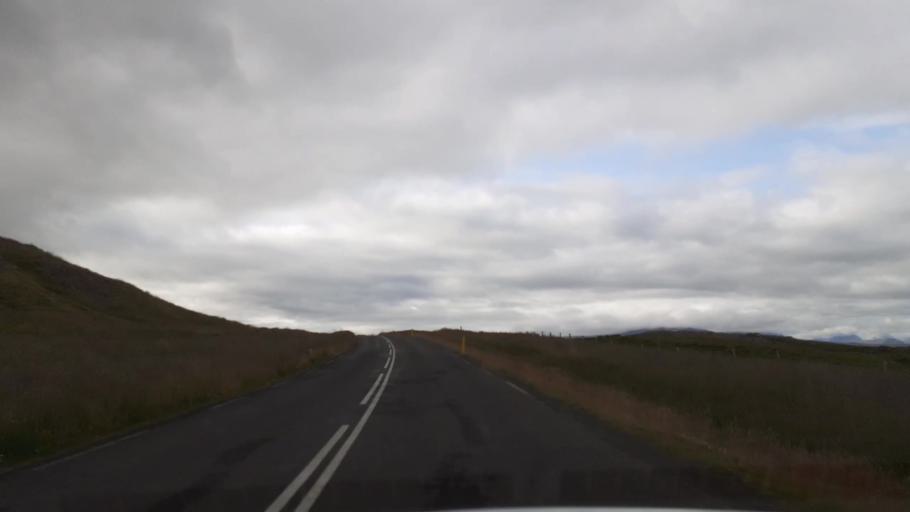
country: IS
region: Northeast
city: Akureyri
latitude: 65.8085
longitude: -18.0559
